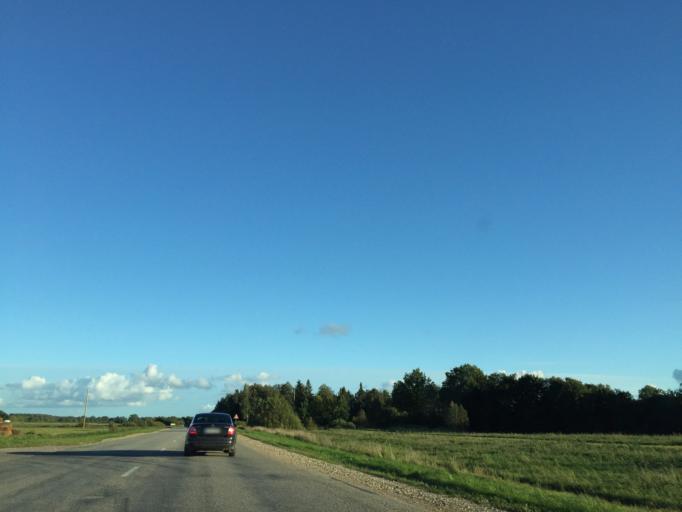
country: LV
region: Kuldigas Rajons
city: Kuldiga
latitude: 56.9555
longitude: 22.0074
